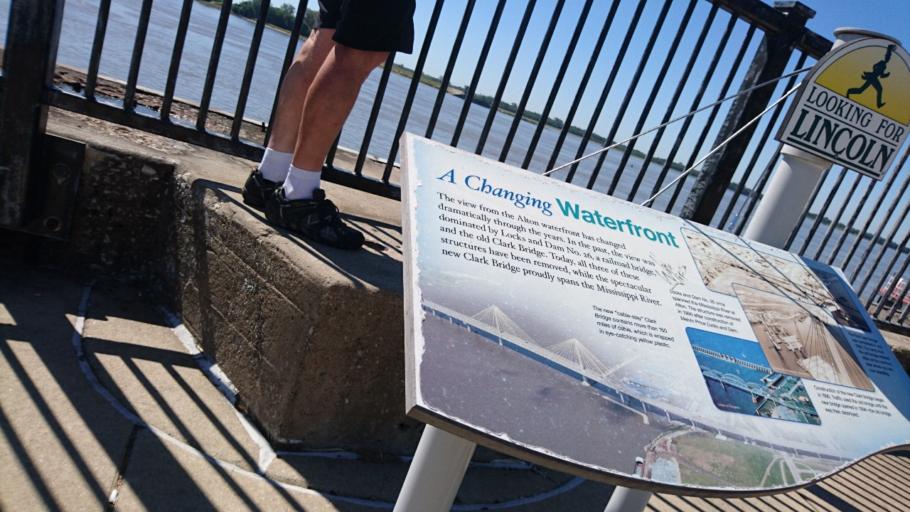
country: US
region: Illinois
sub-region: Madison County
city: Alton
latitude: 38.8861
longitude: -90.1820
